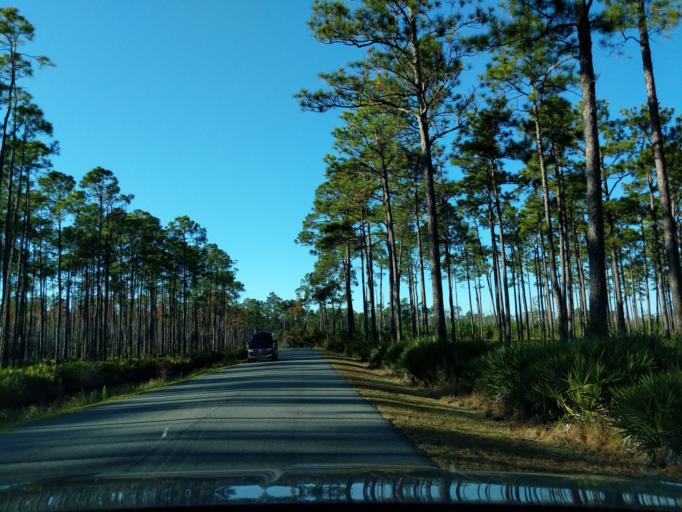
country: US
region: Georgia
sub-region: Charlton County
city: Folkston
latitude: 30.7101
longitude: -82.1519
